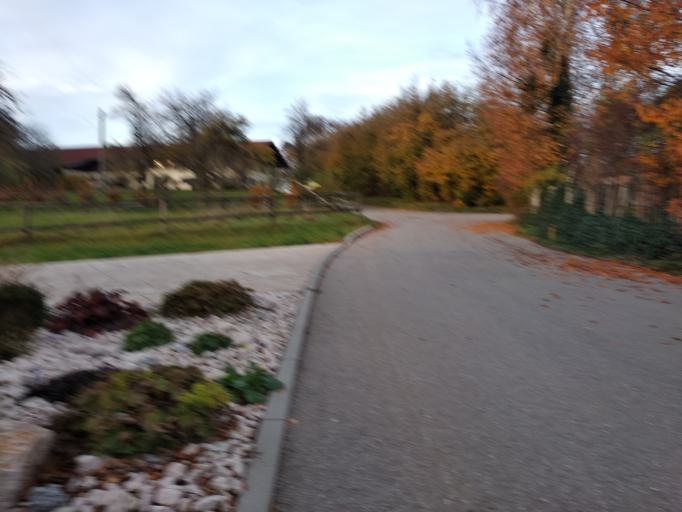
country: DE
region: Bavaria
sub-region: Upper Bavaria
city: Grafing bei Munchen
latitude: 48.0348
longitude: 11.9874
